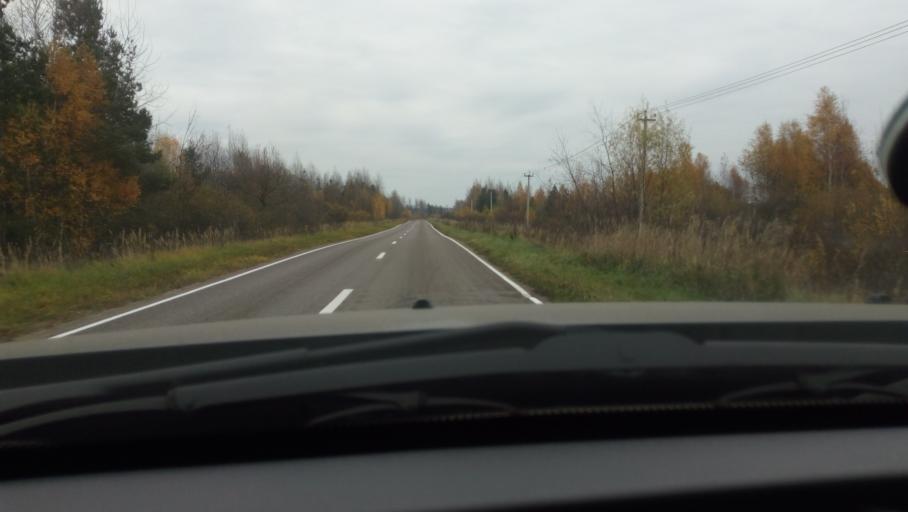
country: RU
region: Moskovskaya
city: Avsyunino
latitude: 55.5950
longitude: 39.2490
